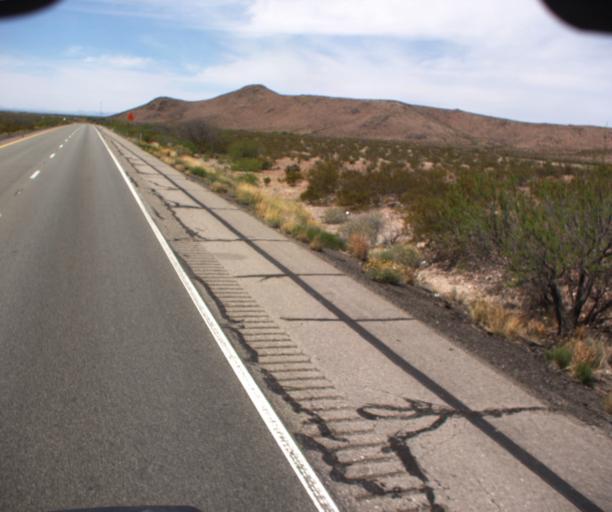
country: US
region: New Mexico
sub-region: Hidalgo County
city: Lordsburg
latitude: 32.2360
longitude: -109.0773
